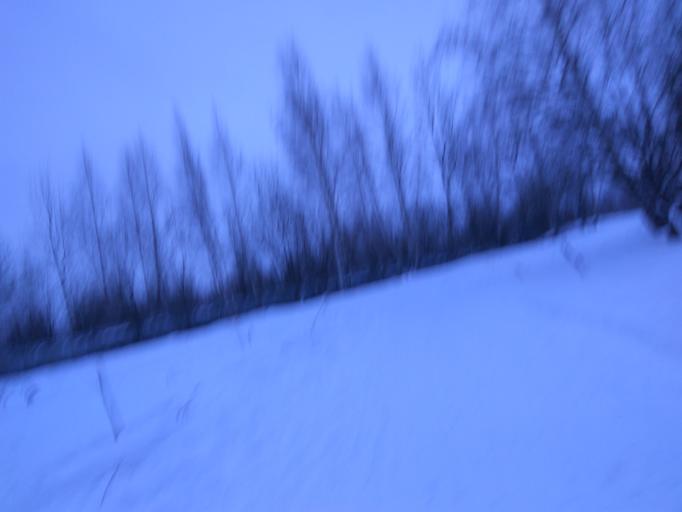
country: RU
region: Moscow
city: Orekhovo-Borisovo
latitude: 55.5968
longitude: 37.7097
